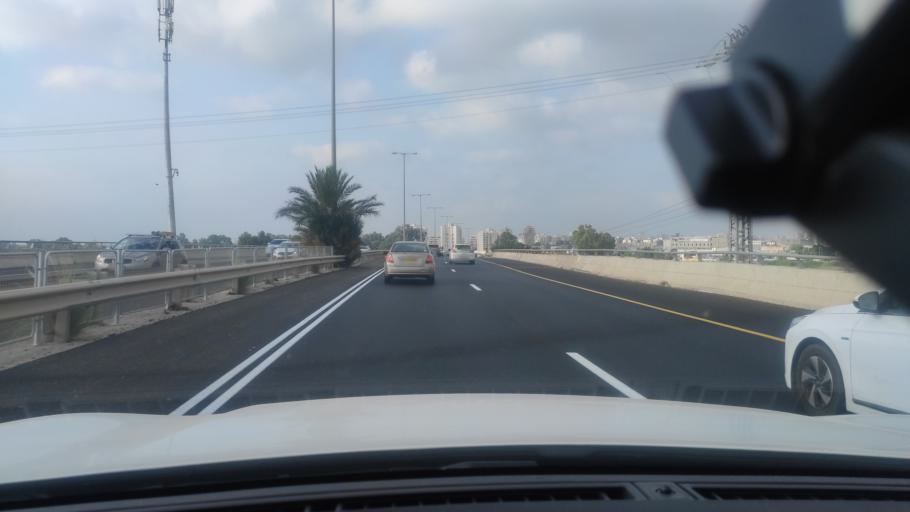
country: IL
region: Central District
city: Petah Tiqwa
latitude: 32.1123
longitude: 34.9027
